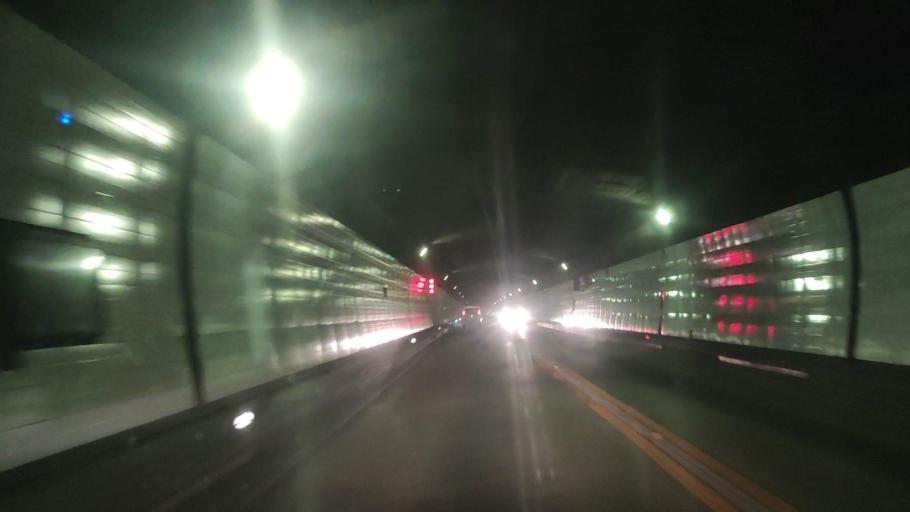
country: JP
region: Kumamoto
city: Hitoyoshi
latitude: 32.0992
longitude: 130.8038
